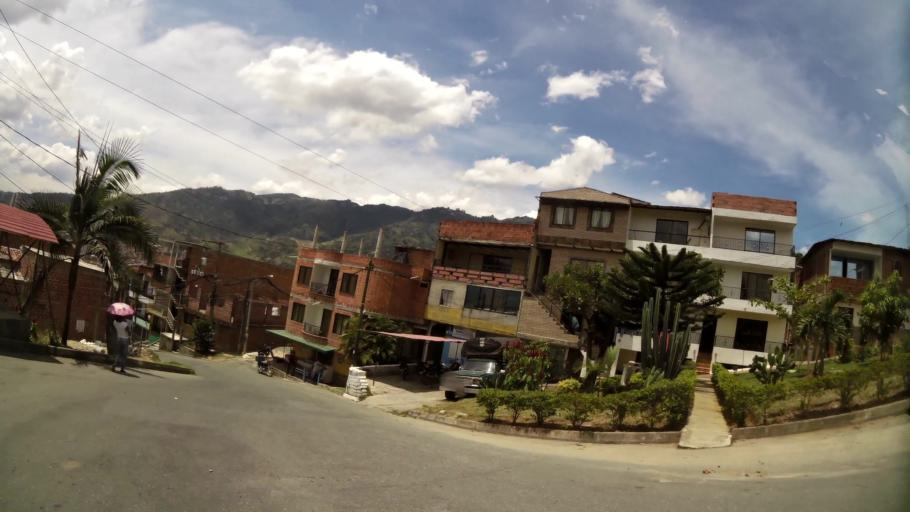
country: CO
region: Antioquia
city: Bello
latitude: 6.3505
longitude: -75.5605
